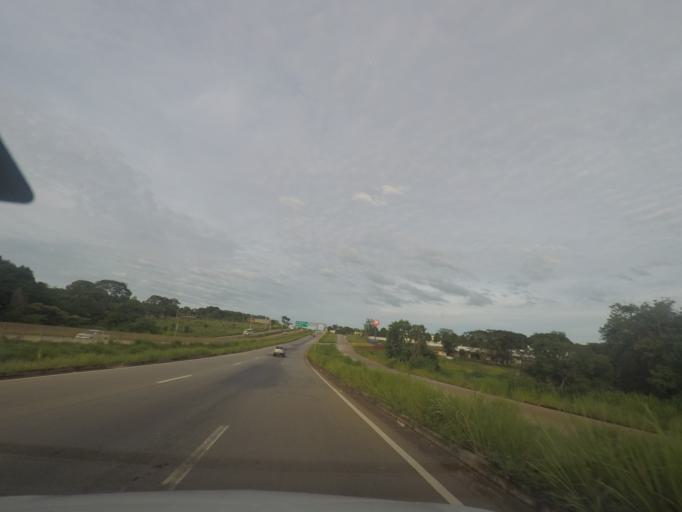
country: BR
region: Goias
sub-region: Trindade
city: Trindade
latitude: -16.7308
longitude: -49.3923
